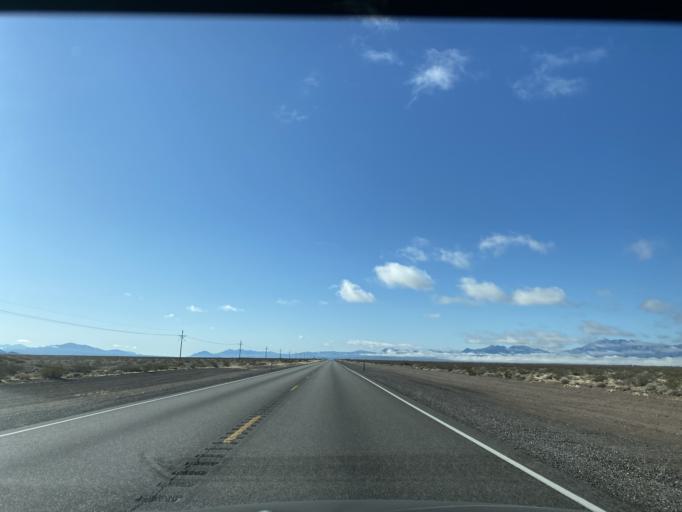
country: US
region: Nevada
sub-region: Nye County
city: Beatty
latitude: 36.6278
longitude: -116.4032
